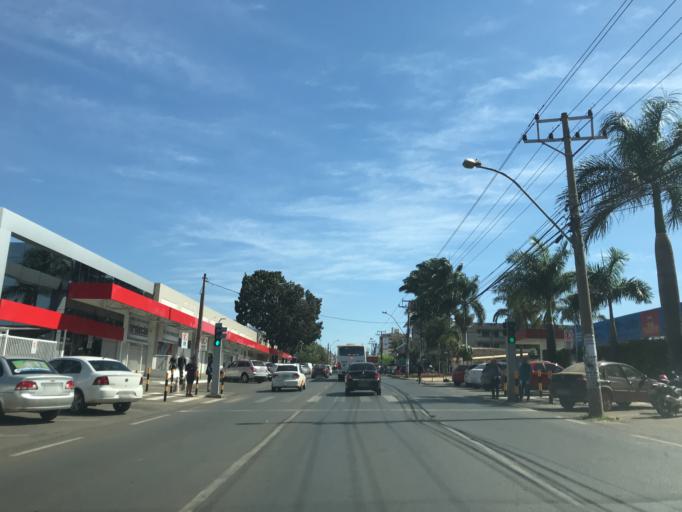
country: BR
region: Federal District
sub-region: Brasilia
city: Brasilia
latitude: -15.8210
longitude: -48.0650
